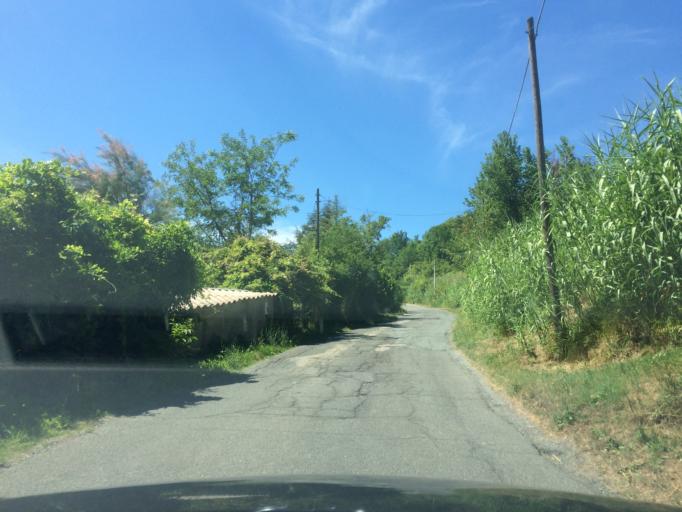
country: IT
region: Piedmont
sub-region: Provincia di Alessandria
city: Acqui Terme
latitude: 44.6871
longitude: 8.4587
